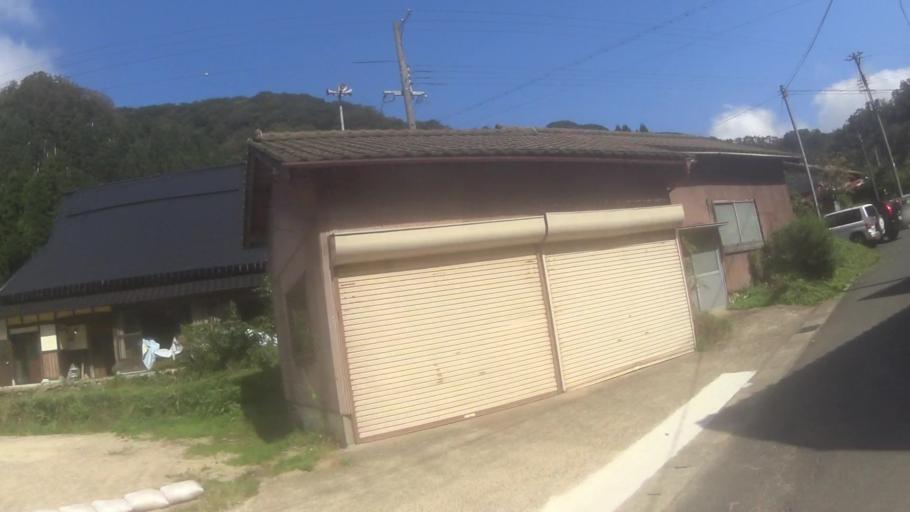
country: JP
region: Kyoto
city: Miyazu
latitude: 35.6812
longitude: 135.1684
